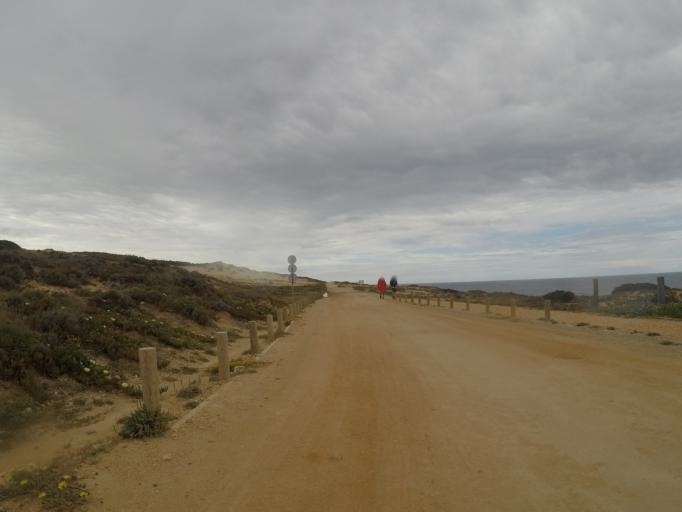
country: PT
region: Beja
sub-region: Odemira
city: Vila Nova de Milfontes
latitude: 37.6481
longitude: -8.8046
